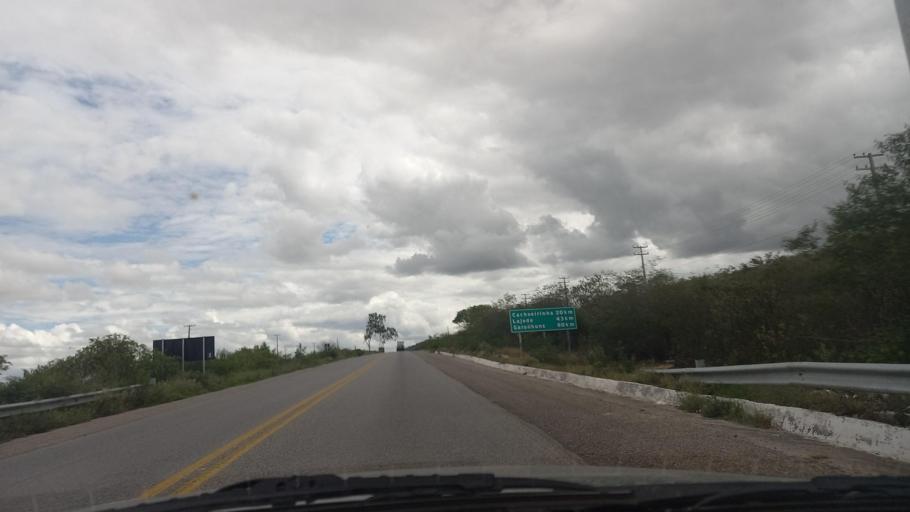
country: BR
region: Pernambuco
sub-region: Cachoeirinha
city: Cachoeirinha
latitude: -8.3325
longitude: -36.1500
